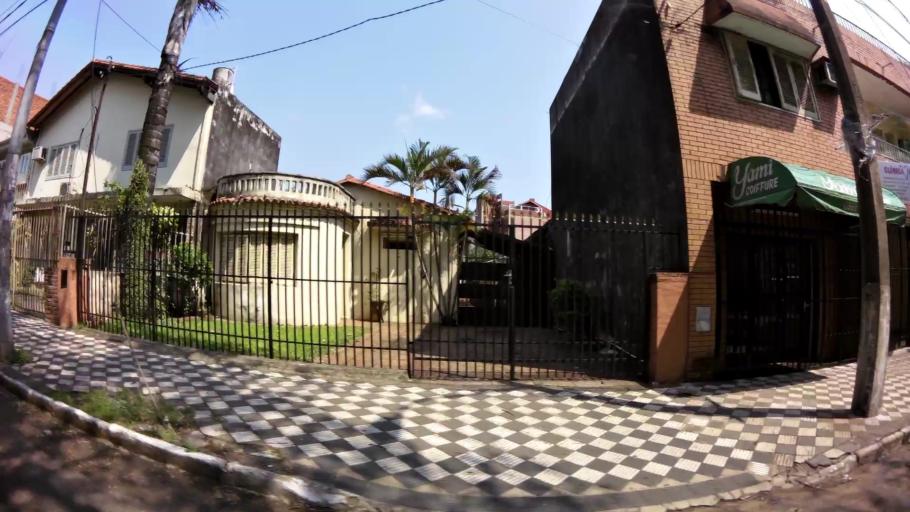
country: PY
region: Asuncion
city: Asuncion
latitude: -25.2978
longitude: -57.6336
